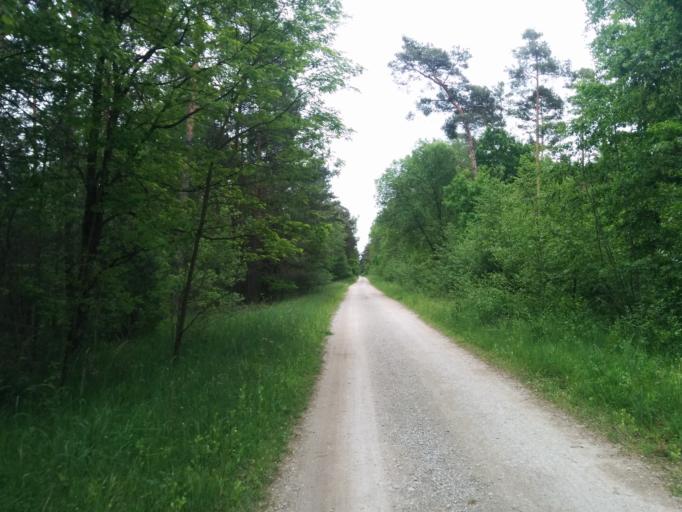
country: DE
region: Bavaria
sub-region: Regierungsbezirk Mittelfranken
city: Buckenhof
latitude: 49.5540
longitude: 11.0403
